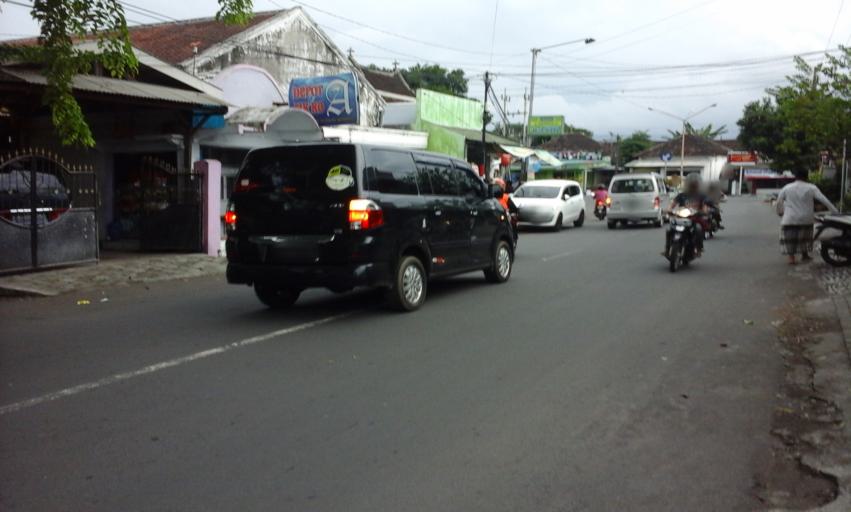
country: ID
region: East Java
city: Lumajang
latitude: -8.1292
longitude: 113.2305
